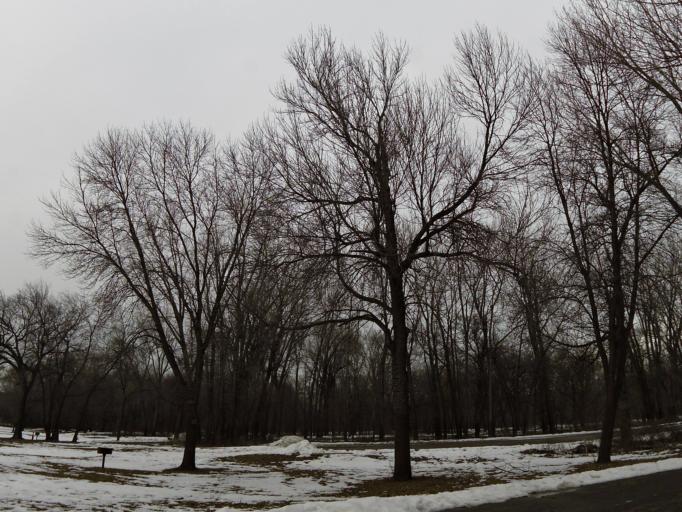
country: US
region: Minnesota
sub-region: Dakota County
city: Mendota Heights
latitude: 44.8811
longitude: -93.1809
